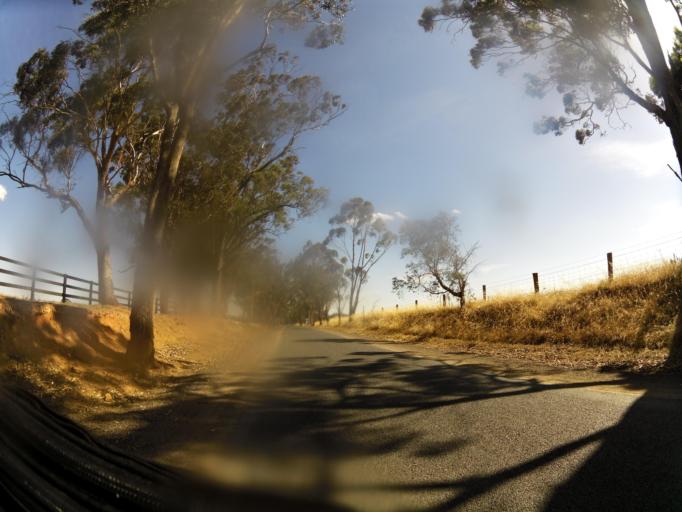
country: AU
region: Victoria
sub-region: Campaspe
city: Kyabram
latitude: -36.8605
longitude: 145.0882
